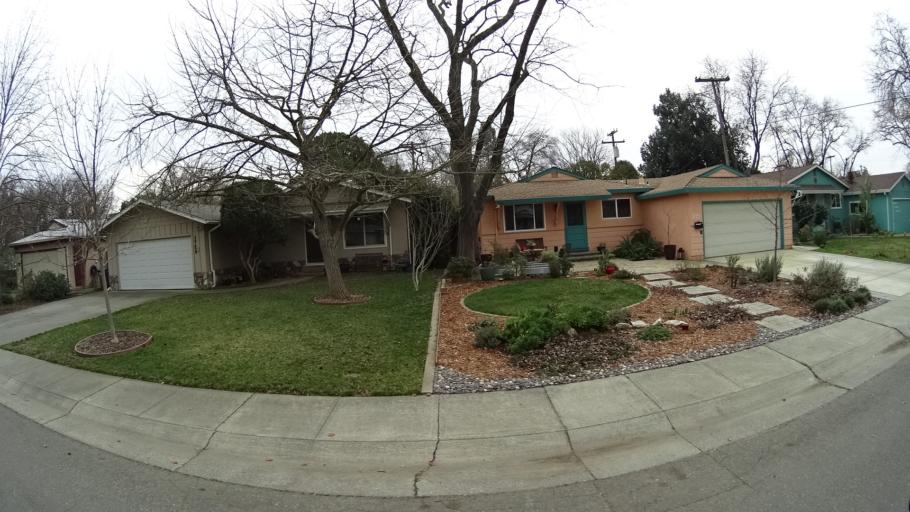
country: US
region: California
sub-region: Yolo County
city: Davis
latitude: 38.5609
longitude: -121.7293
